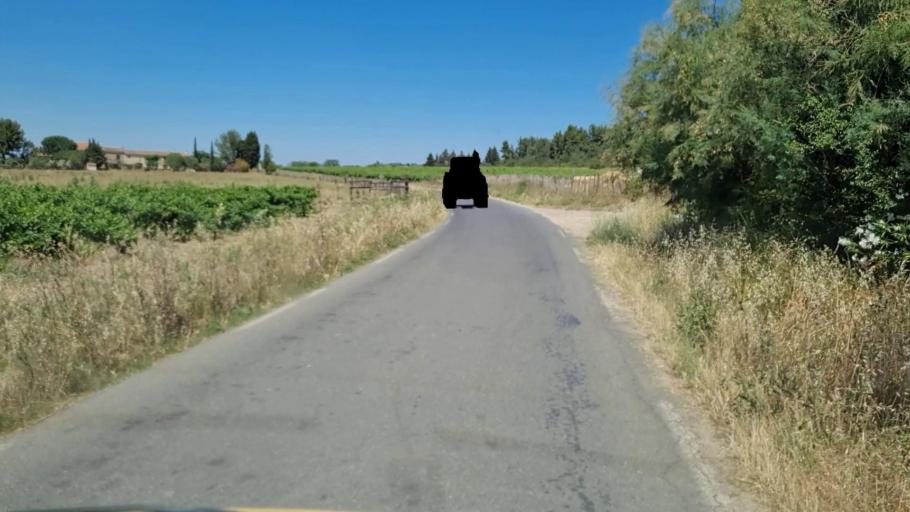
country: FR
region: Languedoc-Roussillon
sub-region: Departement du Gard
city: Le Cailar
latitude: 43.6654
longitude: 4.2587
